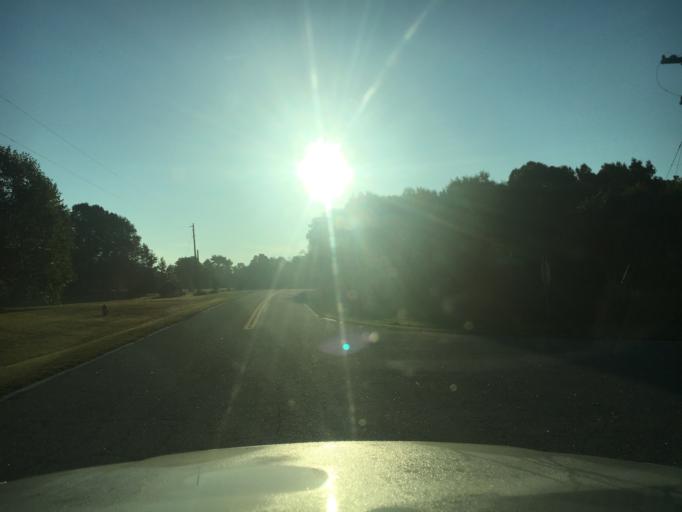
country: US
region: South Carolina
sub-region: Spartanburg County
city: Woodruff
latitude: 34.7876
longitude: -81.9986
